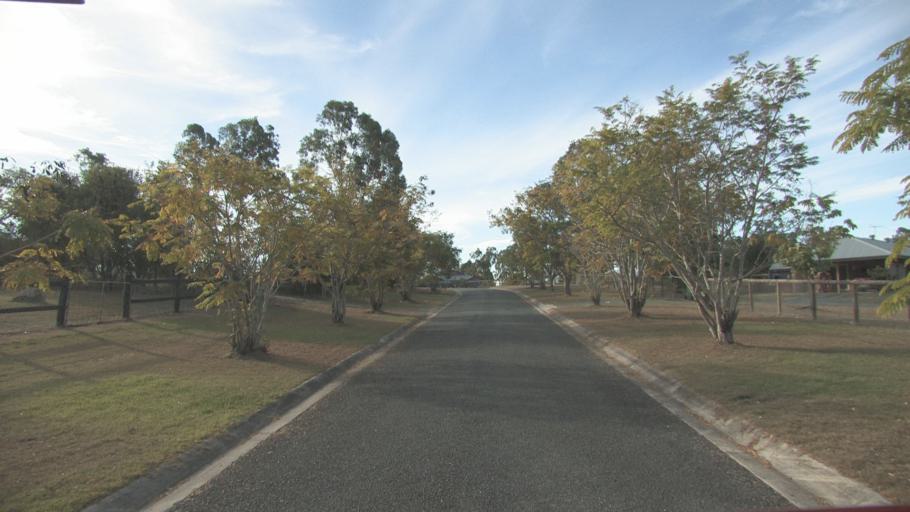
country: AU
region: Queensland
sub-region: Logan
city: North Maclean
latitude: -27.8018
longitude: 152.9643
